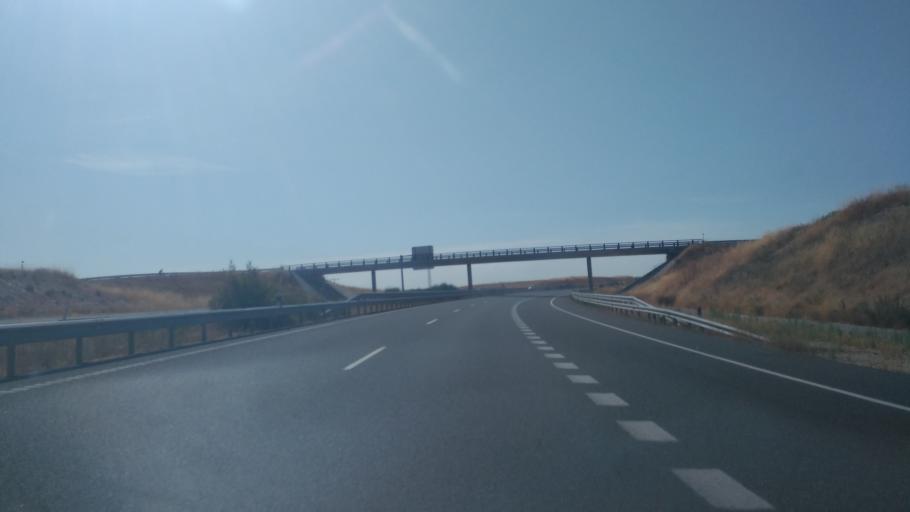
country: ES
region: Castille and Leon
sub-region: Provincia de Salamanca
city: Pelabravo
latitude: 40.9417
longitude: -5.5960
